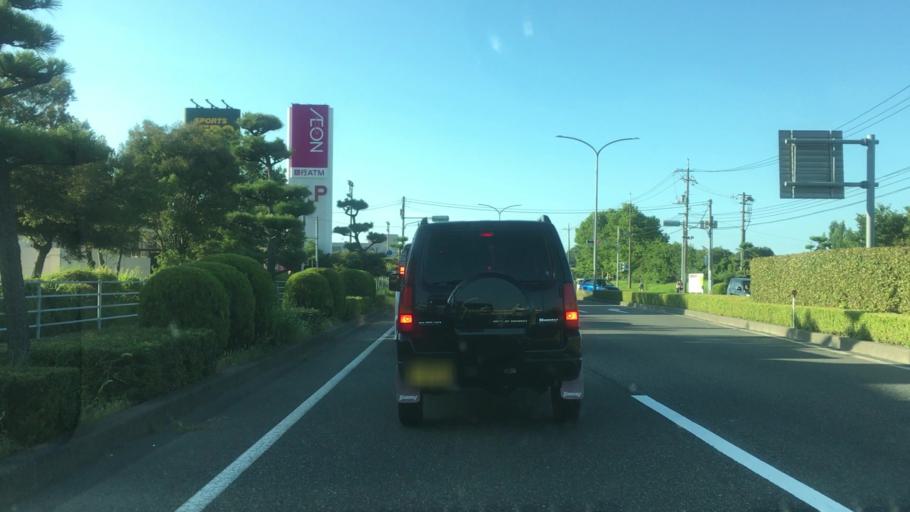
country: JP
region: Tottori
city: Tottori
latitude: 35.5217
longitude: 134.2025
